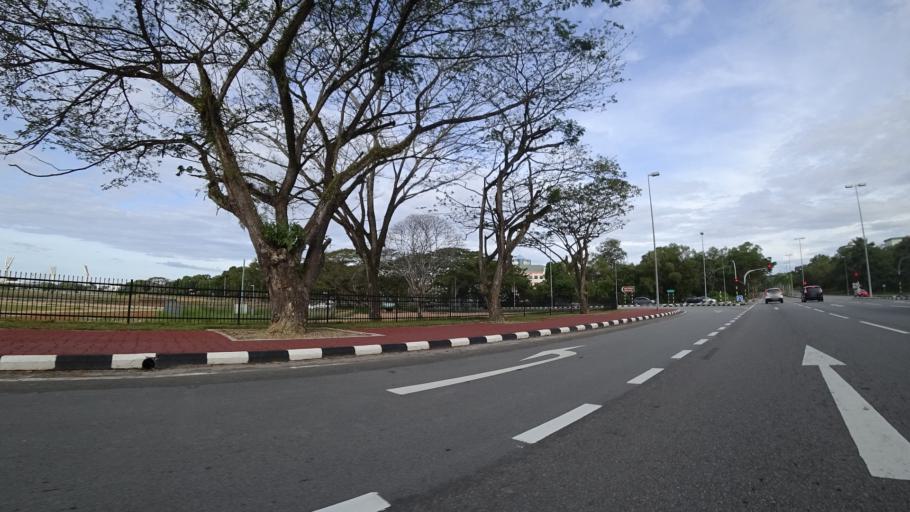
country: BN
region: Brunei and Muara
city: Bandar Seri Begawan
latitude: 4.9205
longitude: 114.9429
